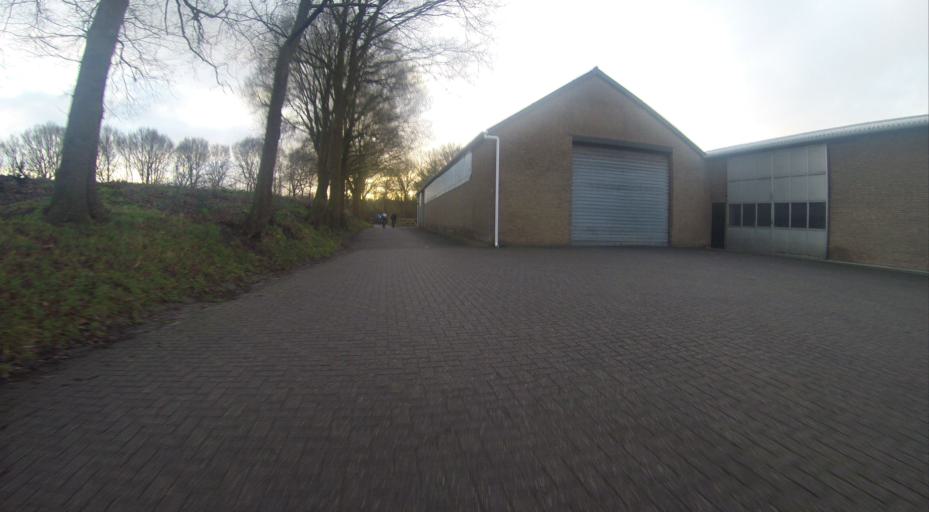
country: NL
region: Overijssel
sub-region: Gemeente Hof van Twente
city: Markelo
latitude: 52.2750
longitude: 6.4244
